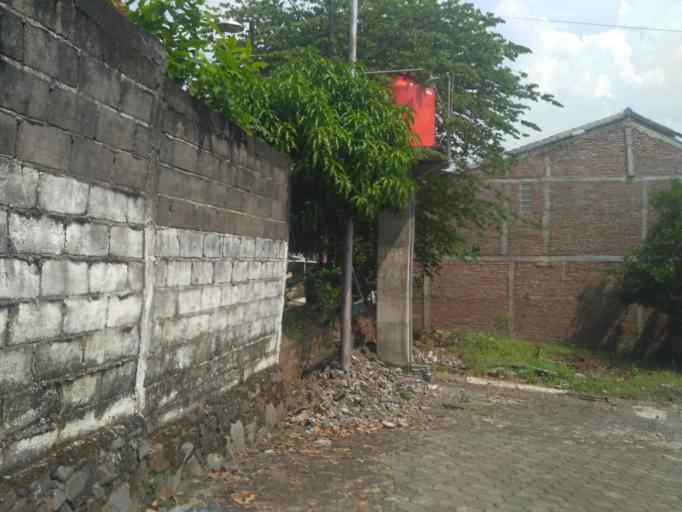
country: ID
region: Central Java
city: Ungaran
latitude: -7.0737
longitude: 110.4400
